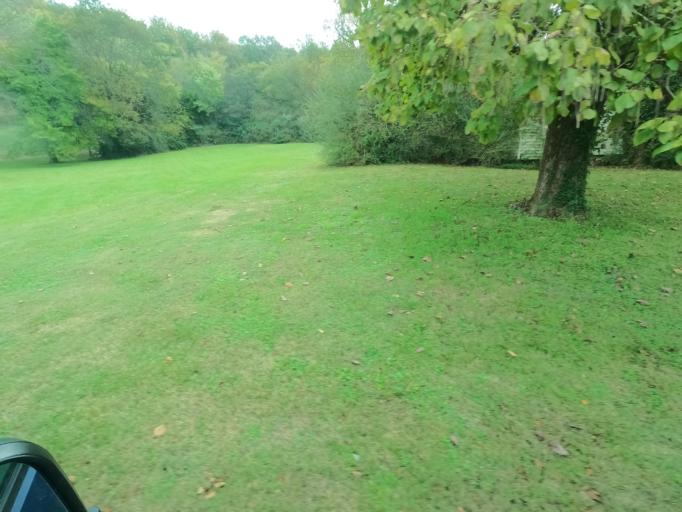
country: US
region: Tennessee
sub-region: Cheatham County
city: Pegram
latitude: 36.1009
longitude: -87.0508
